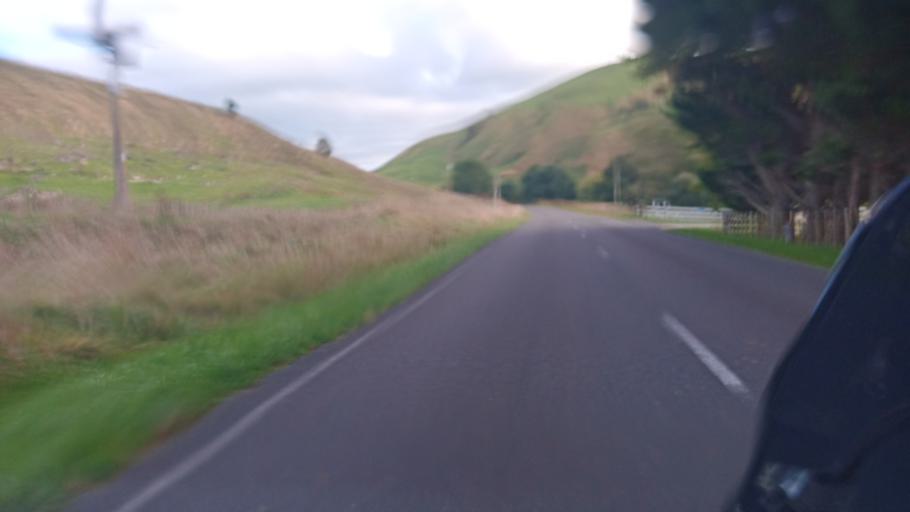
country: NZ
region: Gisborne
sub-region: Gisborne District
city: Gisborne
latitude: -38.5728
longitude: 177.7362
